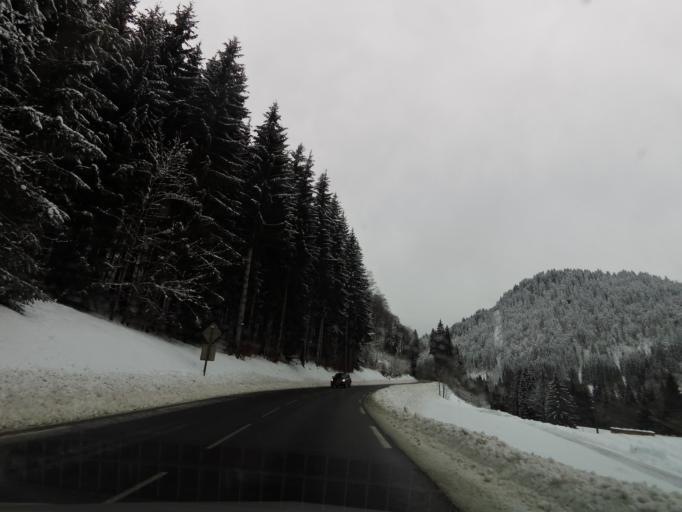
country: FR
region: Rhone-Alpes
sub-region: Departement de la Haute-Savoie
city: Morzine
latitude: 46.1859
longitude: 6.6822
